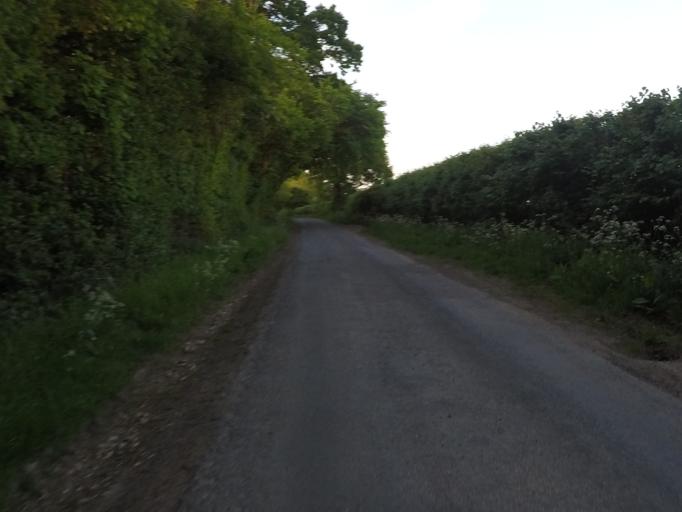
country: GB
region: England
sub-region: Oxfordshire
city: North Leigh
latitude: 51.8304
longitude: -1.4751
